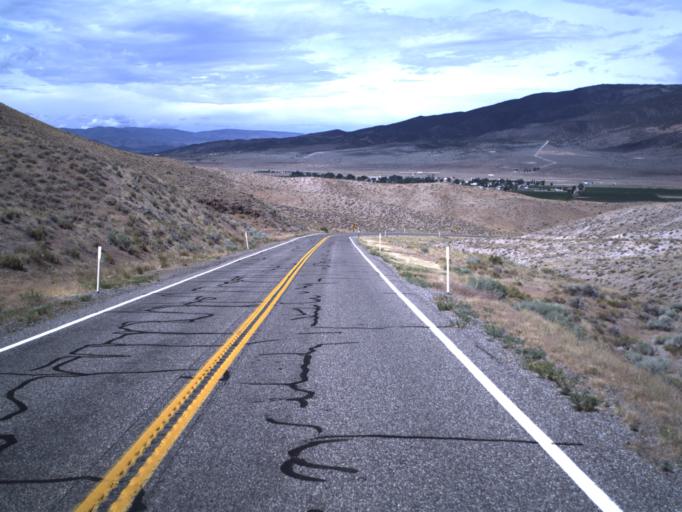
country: US
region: Utah
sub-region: Sevier County
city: Monroe
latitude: 38.6316
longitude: -112.1822
